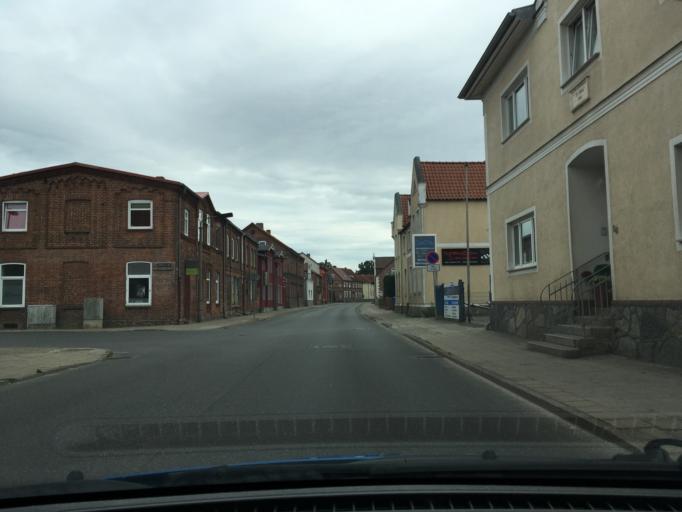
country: DE
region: Mecklenburg-Vorpommern
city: Wittenburg
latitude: 53.5097
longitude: 11.0771
